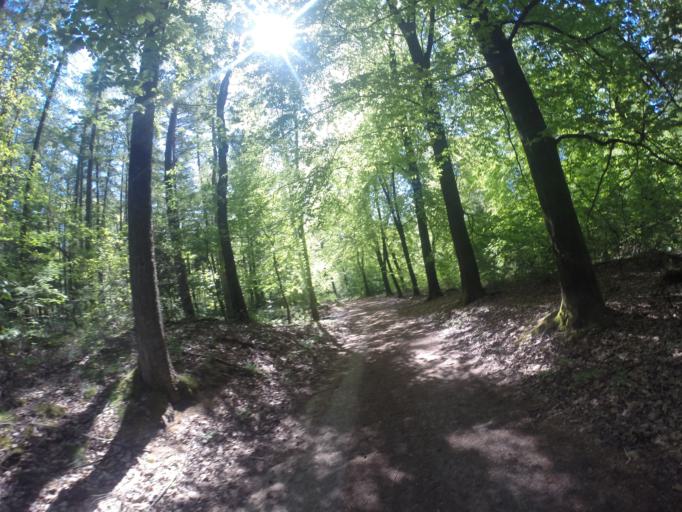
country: NL
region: Gelderland
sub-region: Gemeente Montferland
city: s-Heerenberg
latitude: 51.9101
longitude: 6.2460
